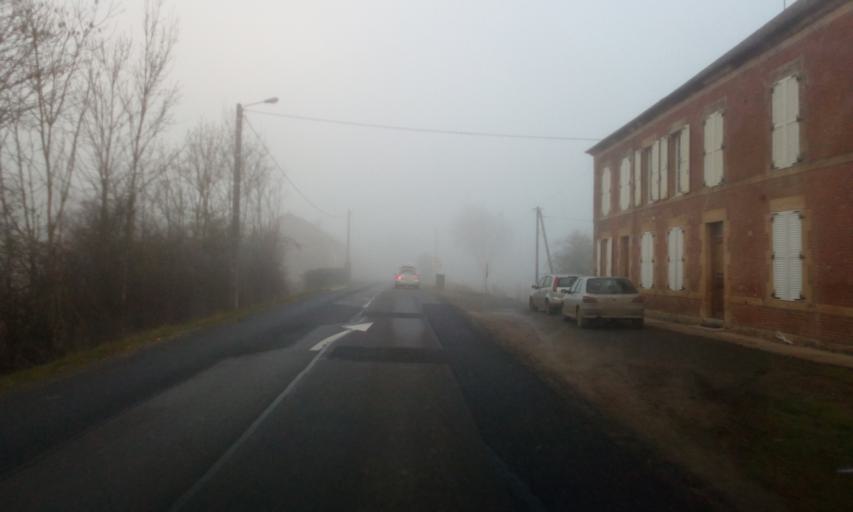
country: FR
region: Champagne-Ardenne
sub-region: Departement des Ardennes
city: Rimogne
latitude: 49.7988
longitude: 4.5243
